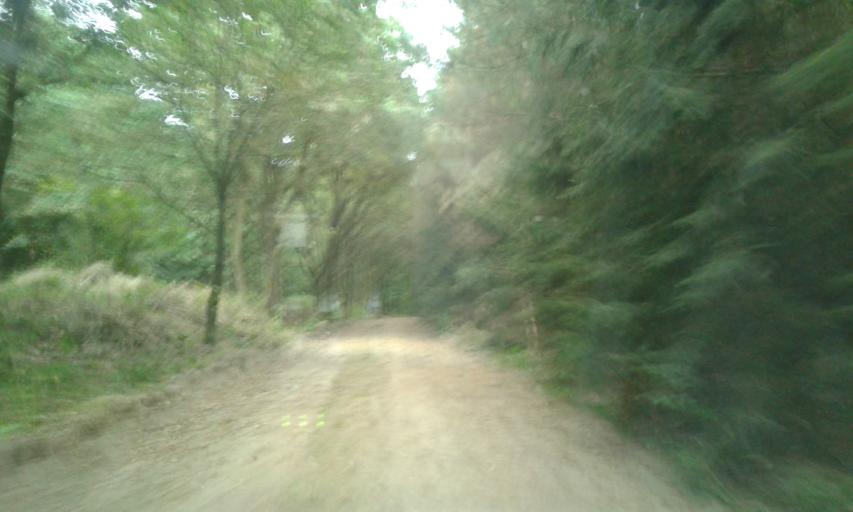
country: PL
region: West Pomeranian Voivodeship
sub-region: Powiat stargardzki
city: Dolice
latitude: 53.1827
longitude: 15.2384
